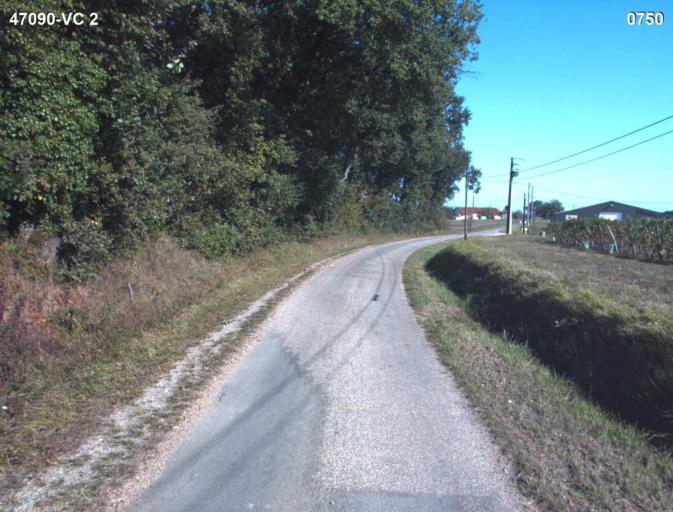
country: FR
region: Aquitaine
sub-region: Departement du Lot-et-Garonne
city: Vianne
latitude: 44.1845
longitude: 0.3652
